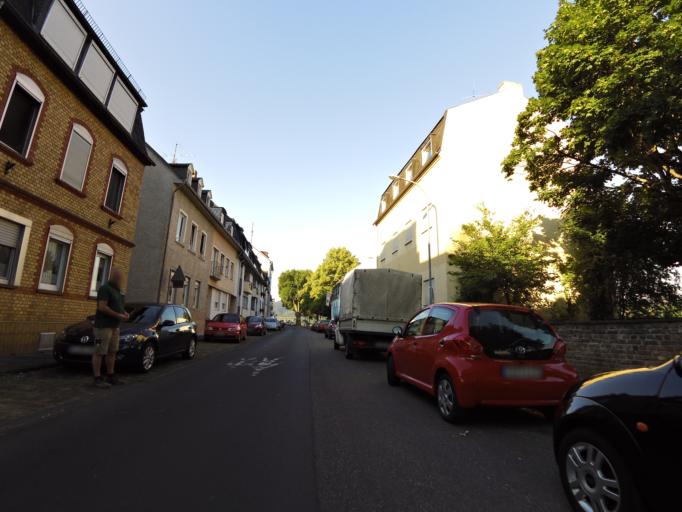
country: DE
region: Rheinland-Pfalz
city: Koblenz
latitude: 50.3445
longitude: 7.6013
